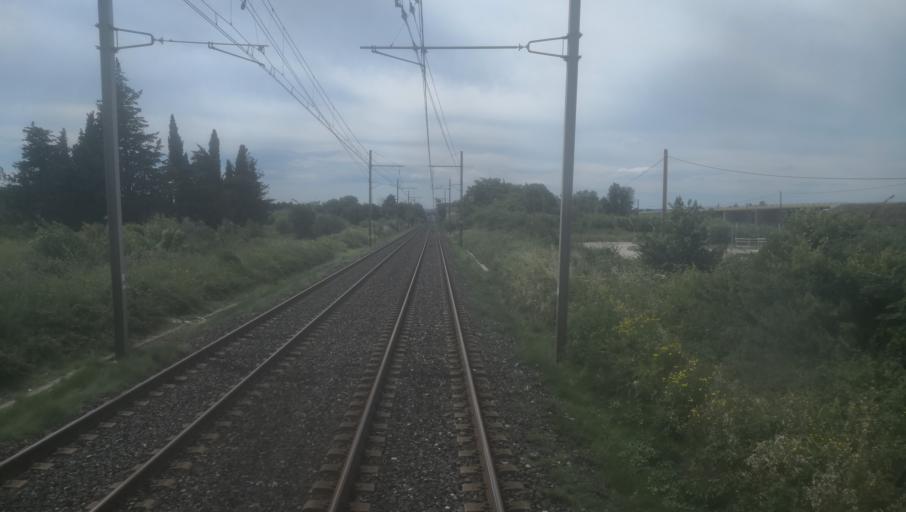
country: FR
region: Languedoc-Roussillon
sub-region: Departement du Gard
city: Manduel
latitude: 43.8274
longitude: 4.4765
